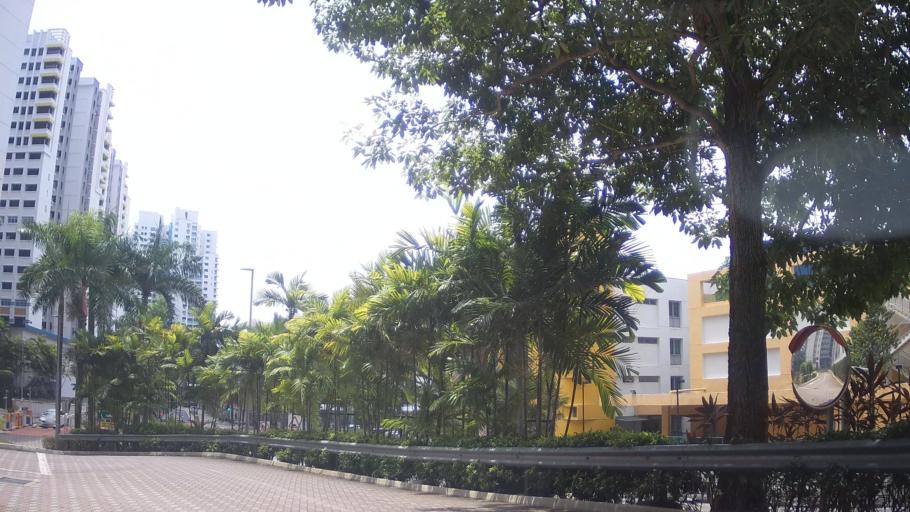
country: MY
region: Johor
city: Johor Bahru
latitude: 1.3844
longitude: 103.7606
